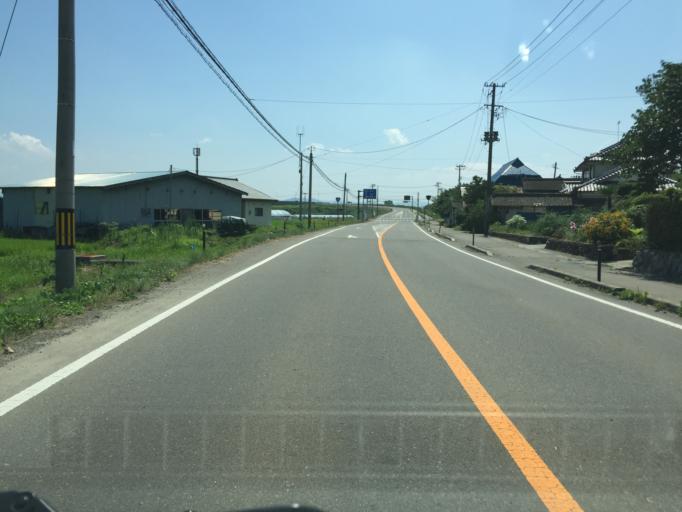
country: JP
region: Fukushima
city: Yanagawamachi-saiwaicho
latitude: 37.8751
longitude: 140.6103
